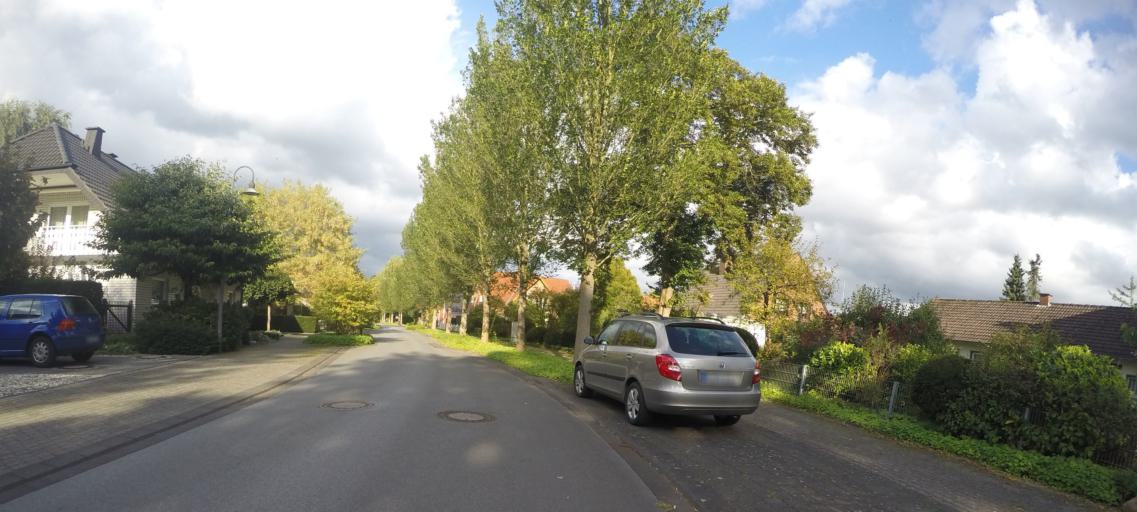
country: DE
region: North Rhine-Westphalia
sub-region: Regierungsbezirk Arnsberg
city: Lippstadt
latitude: 51.6871
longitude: 8.3575
